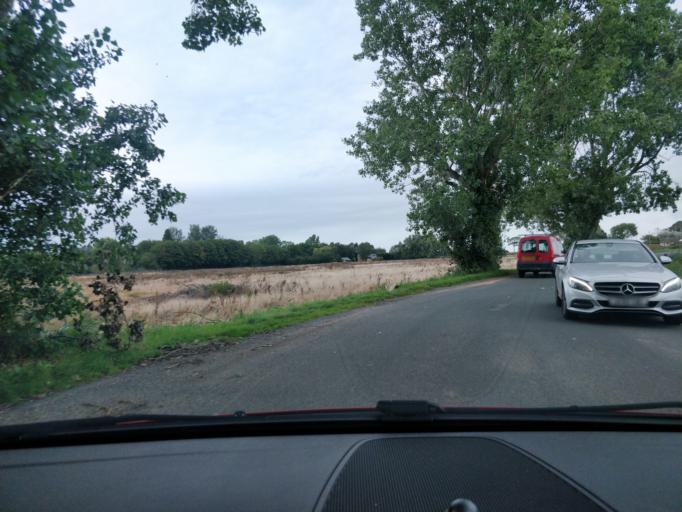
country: GB
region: England
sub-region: Lancashire
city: Ormskirk
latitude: 53.6181
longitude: -2.8595
